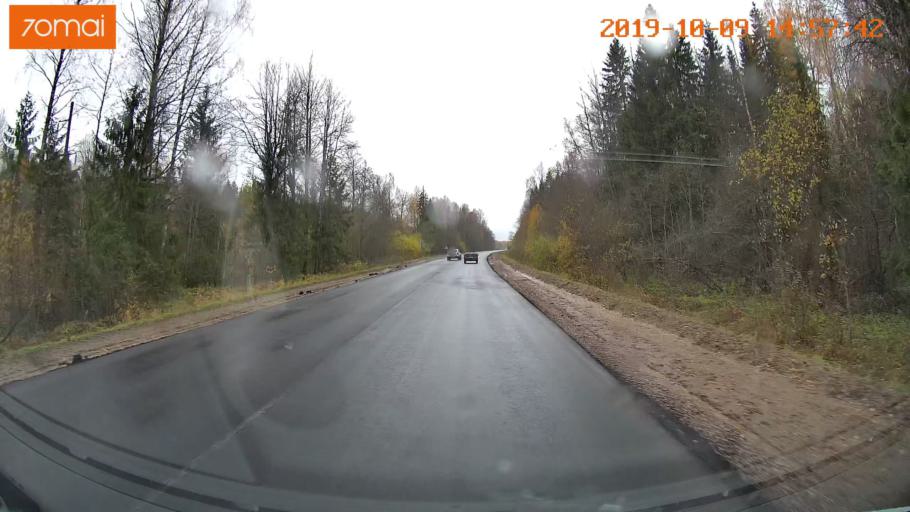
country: RU
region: Kostroma
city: Chistyye Bory
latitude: 58.3349
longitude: 41.6521
